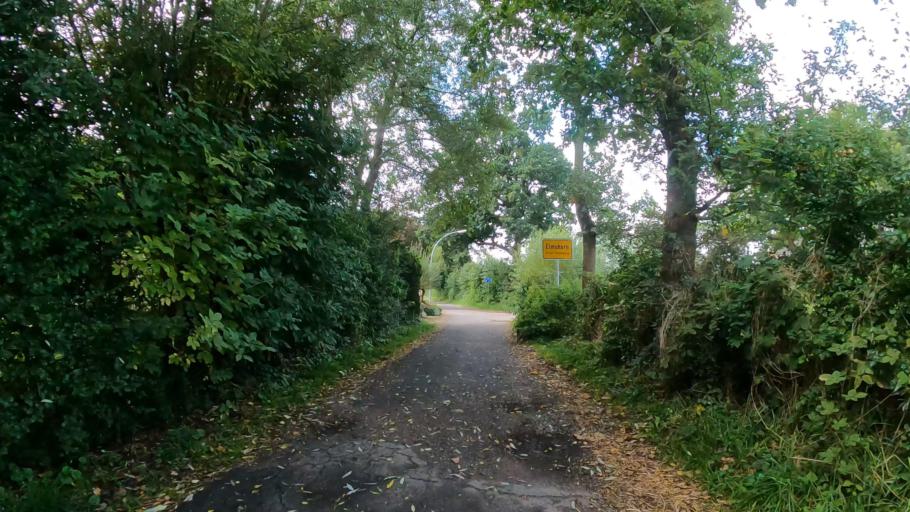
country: DE
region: Schleswig-Holstein
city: Kolln-Reisiek
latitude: 53.7323
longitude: 9.6808
